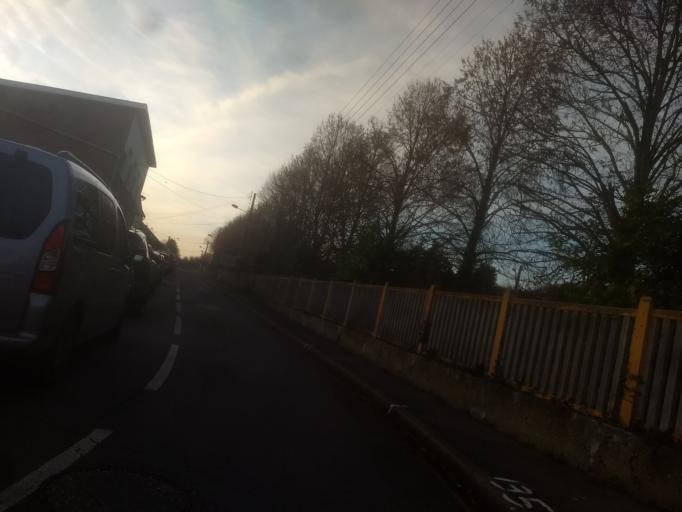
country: FR
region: Nord-Pas-de-Calais
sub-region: Departement du Pas-de-Calais
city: Achicourt
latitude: 50.2779
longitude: 2.7609
